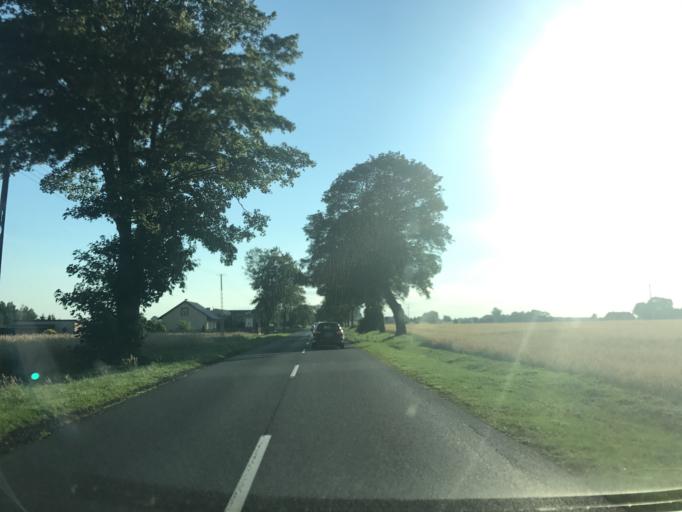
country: PL
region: Greater Poland Voivodeship
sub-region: Powiat koninski
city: Grodziec
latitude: 52.0486
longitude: 18.1030
